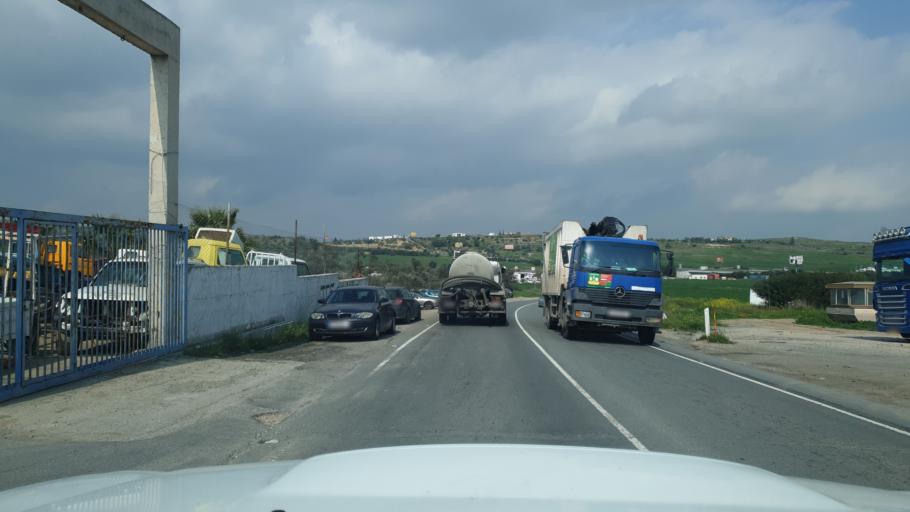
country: CY
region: Lefkosia
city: Dali
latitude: 35.0528
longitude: 33.3818
